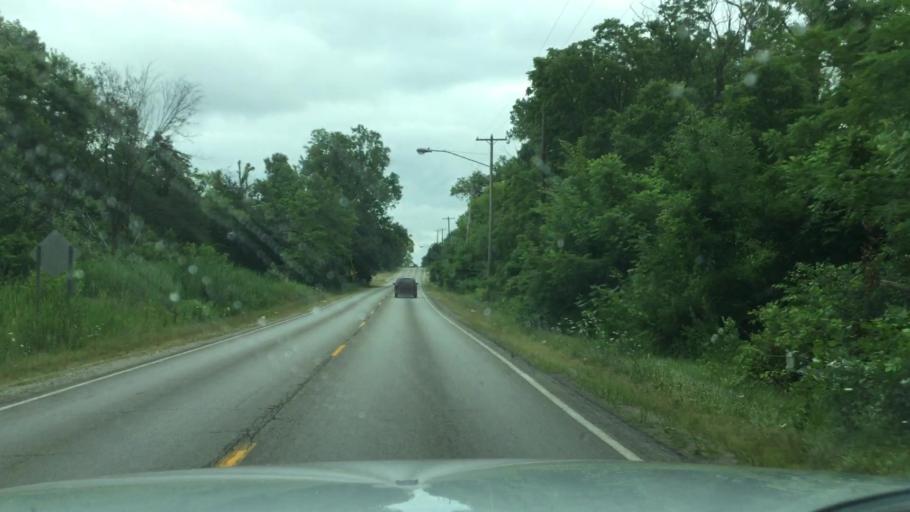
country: US
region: Michigan
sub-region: Genesee County
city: Beecher
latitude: 43.0764
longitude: -83.6528
